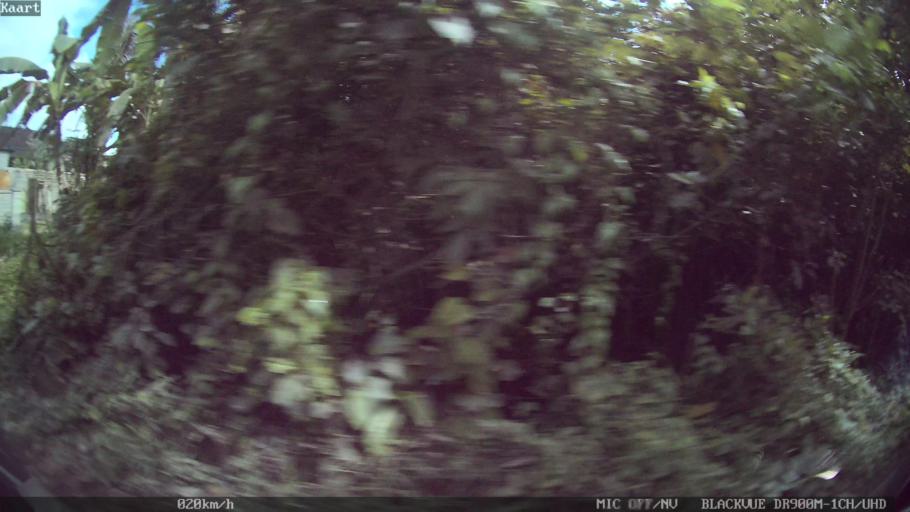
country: ID
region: Bali
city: Banjar Tebongkang
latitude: -8.5398
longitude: 115.2506
